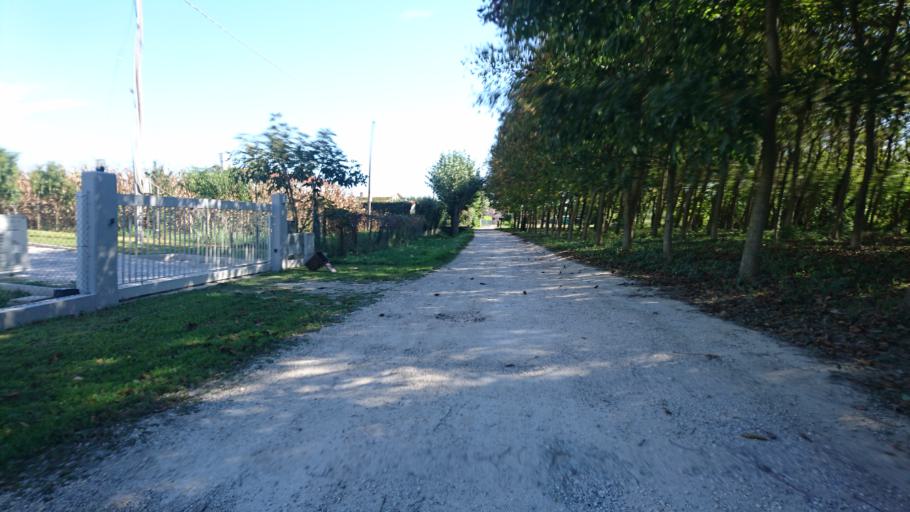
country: IT
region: Veneto
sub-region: Provincia di Padova
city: Oltre Brenta
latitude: 45.3992
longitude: 11.9995
